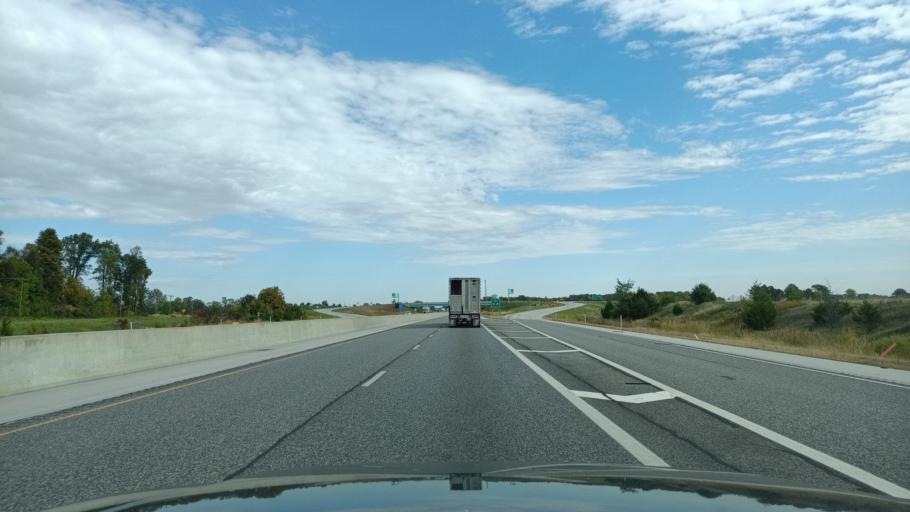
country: US
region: Indiana
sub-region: Wells County
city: Ossian
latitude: 40.9644
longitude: -85.1278
